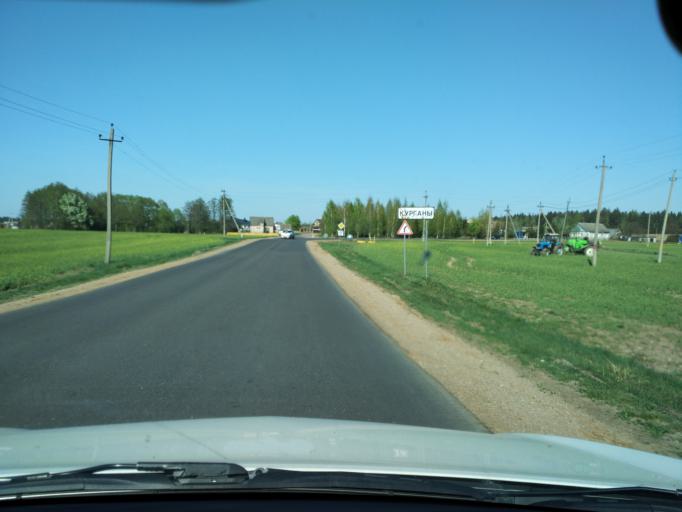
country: BY
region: Minsk
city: Lyeskawka
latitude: 54.0092
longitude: 27.7411
